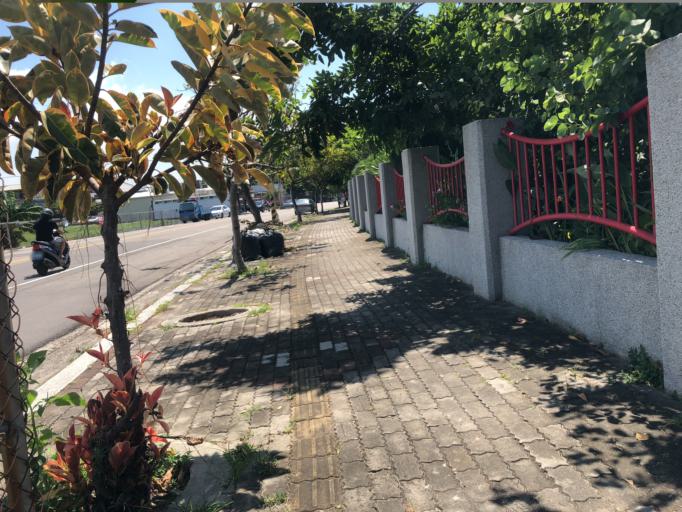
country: TW
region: Taiwan
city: Fengyuan
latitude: 24.2786
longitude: 120.5604
